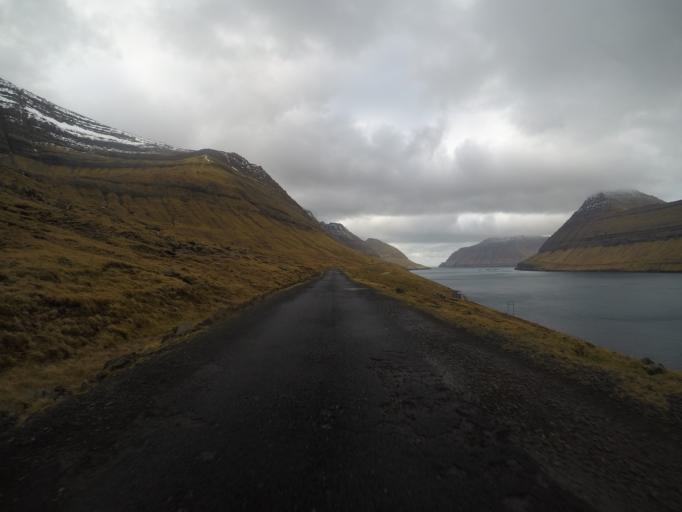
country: FO
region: Nordoyar
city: Klaksvik
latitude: 62.3160
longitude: -6.5545
